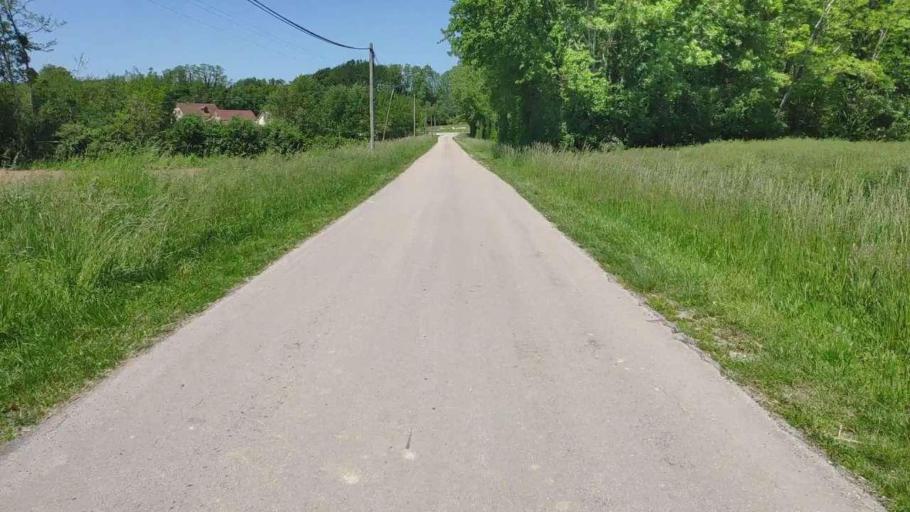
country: FR
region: Franche-Comte
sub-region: Departement du Jura
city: Bletterans
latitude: 46.7599
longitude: 5.4214
